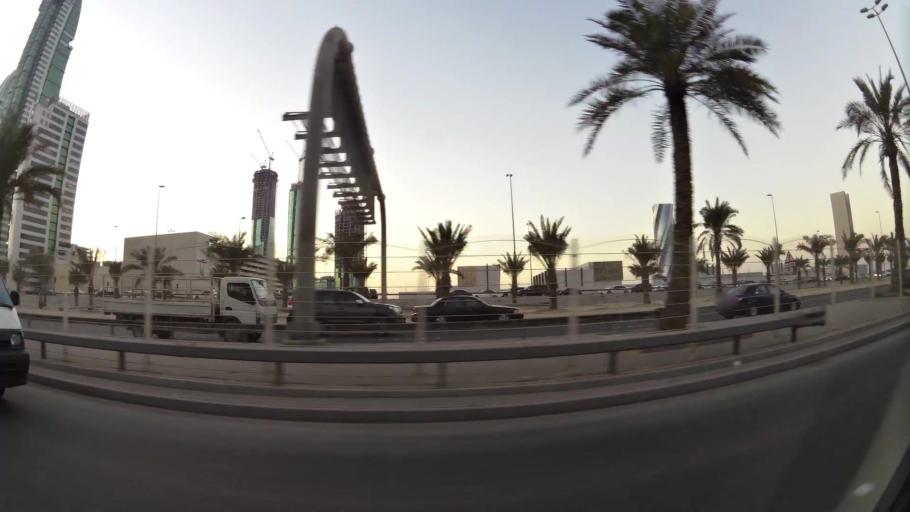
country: BH
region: Manama
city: Manama
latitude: 26.2380
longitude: 50.5775
